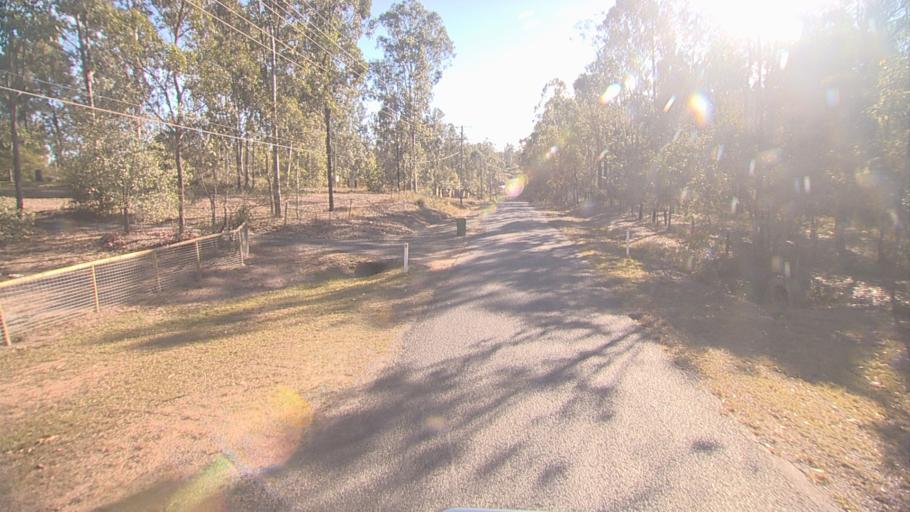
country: AU
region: Queensland
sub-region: Ipswich
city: Springfield Lakes
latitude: -27.6920
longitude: 152.9295
